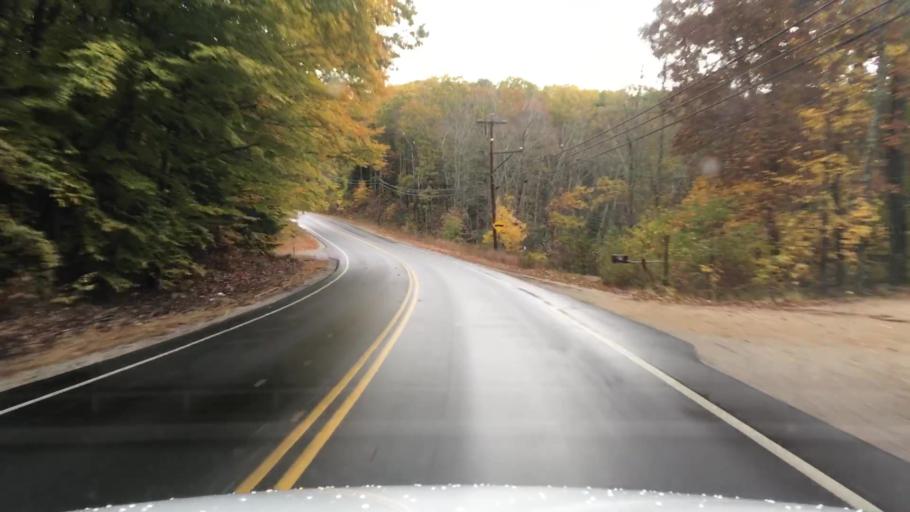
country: US
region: New Hampshire
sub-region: Strafford County
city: Lee
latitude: 43.1247
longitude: -71.0191
